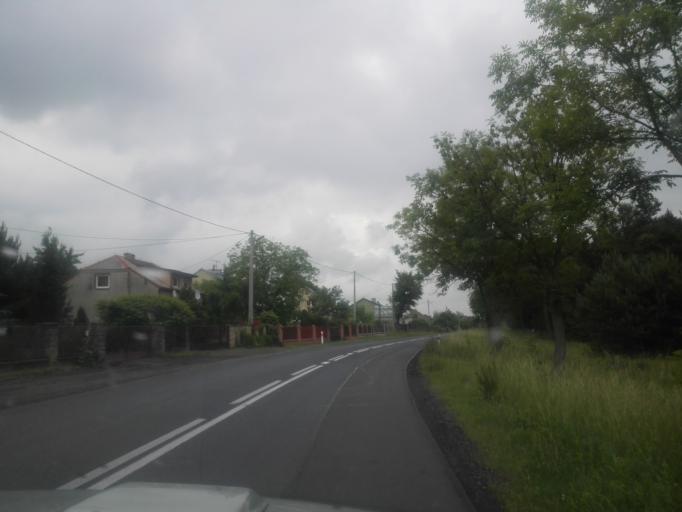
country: PL
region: Silesian Voivodeship
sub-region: Powiat czestochowski
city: Olsztyn
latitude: 50.7534
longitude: 19.3001
